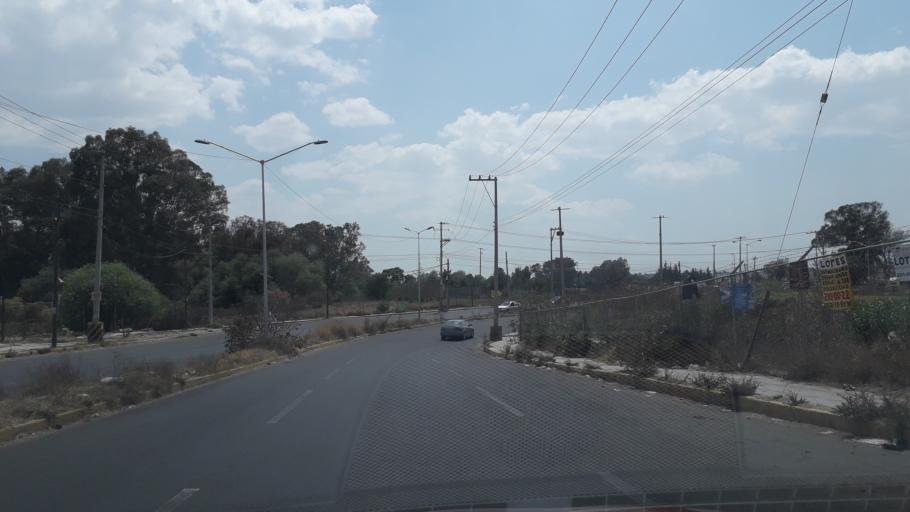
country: MX
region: Puebla
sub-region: Puebla
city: Galaxia la Calera
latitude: 18.9925
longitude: -98.1751
